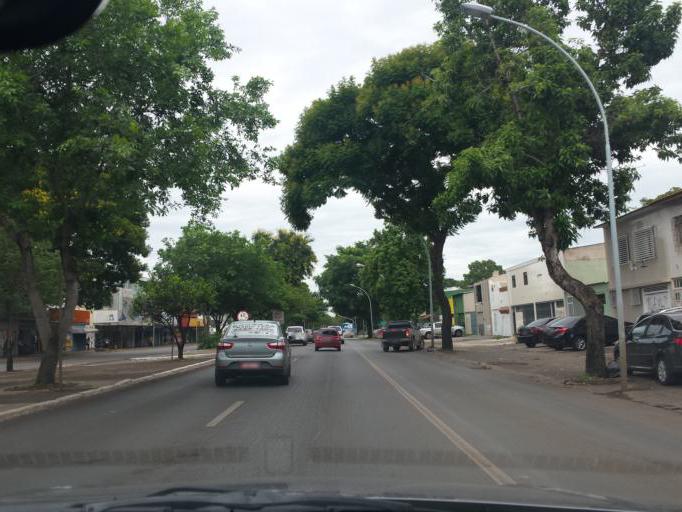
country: BR
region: Federal District
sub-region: Brasilia
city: Brasilia
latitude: -15.8048
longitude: -47.8977
